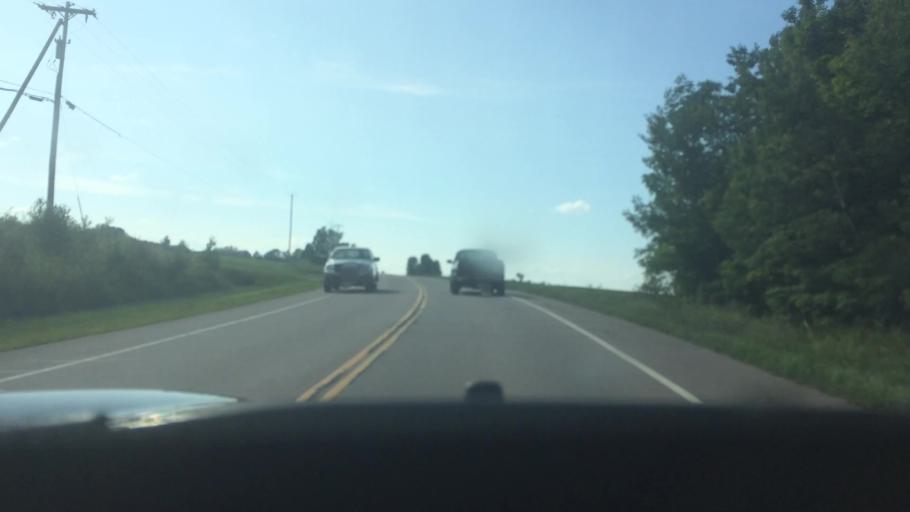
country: US
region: New York
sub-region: Franklin County
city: Malone
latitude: 44.8504
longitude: -74.2019
